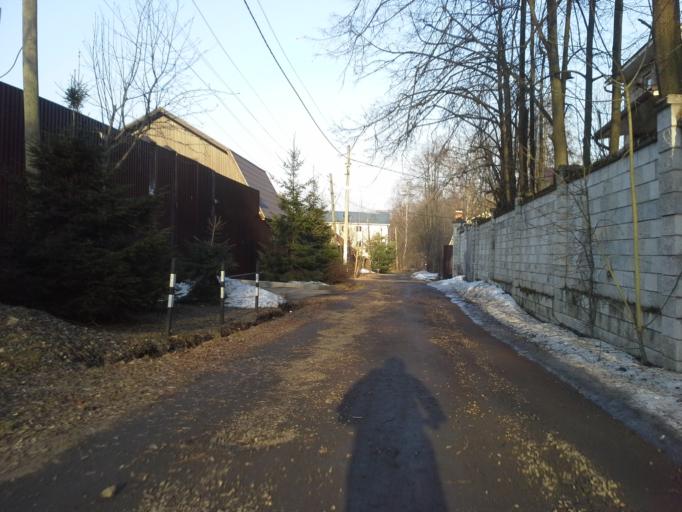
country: RU
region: Moscow
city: Novo-Peredelkino
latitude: 55.6471
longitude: 37.3130
